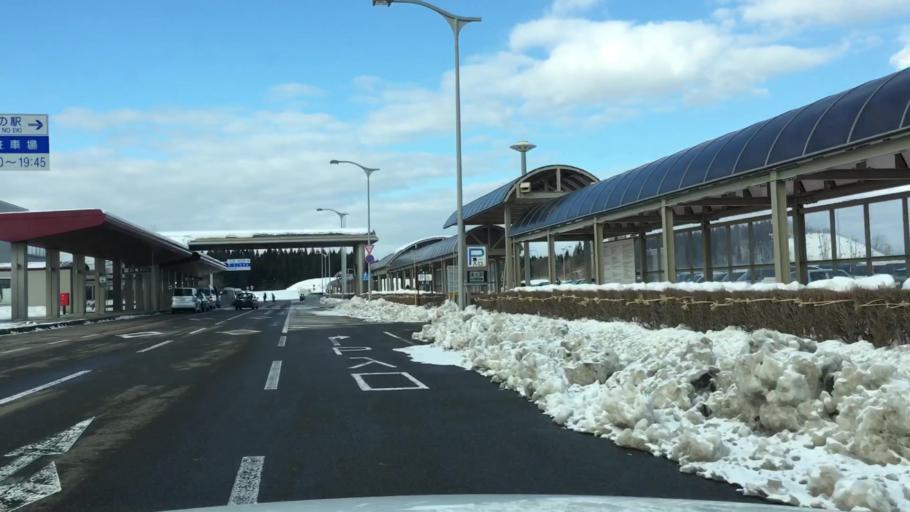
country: JP
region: Akita
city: Takanosu
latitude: 40.1958
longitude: 140.3733
